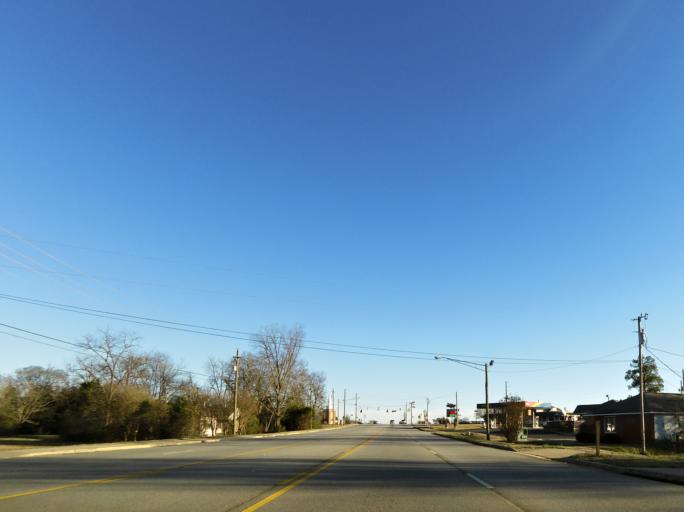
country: US
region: Georgia
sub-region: Houston County
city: Centerville
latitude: 32.6250
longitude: -83.6884
